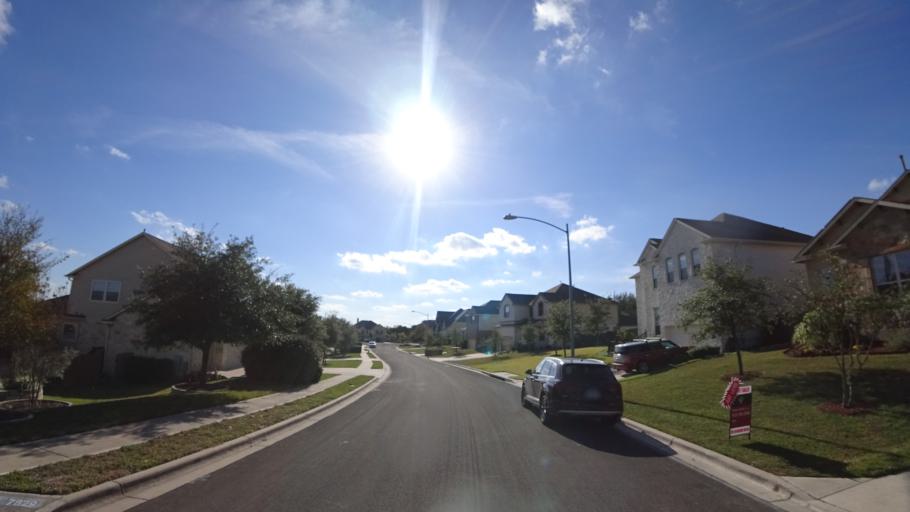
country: US
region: Texas
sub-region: Travis County
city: Barton Creek
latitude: 30.2505
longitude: -97.8800
